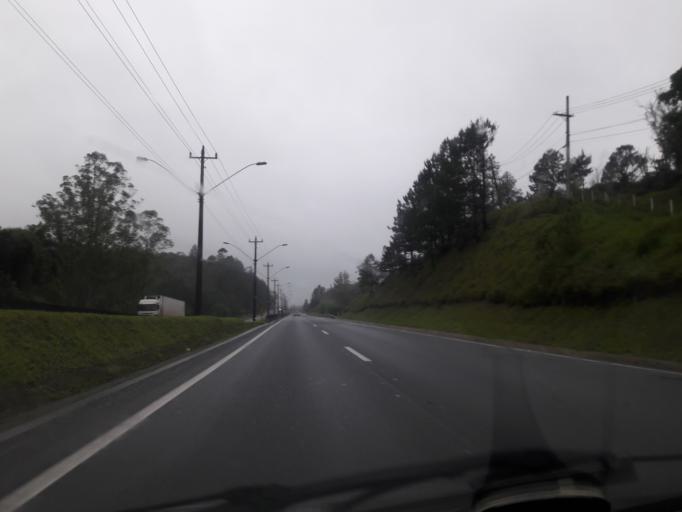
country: BR
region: Sao Paulo
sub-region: Sao Lourenco Da Serra
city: Sao Lourenco da Serra
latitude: -23.8707
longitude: -46.9595
